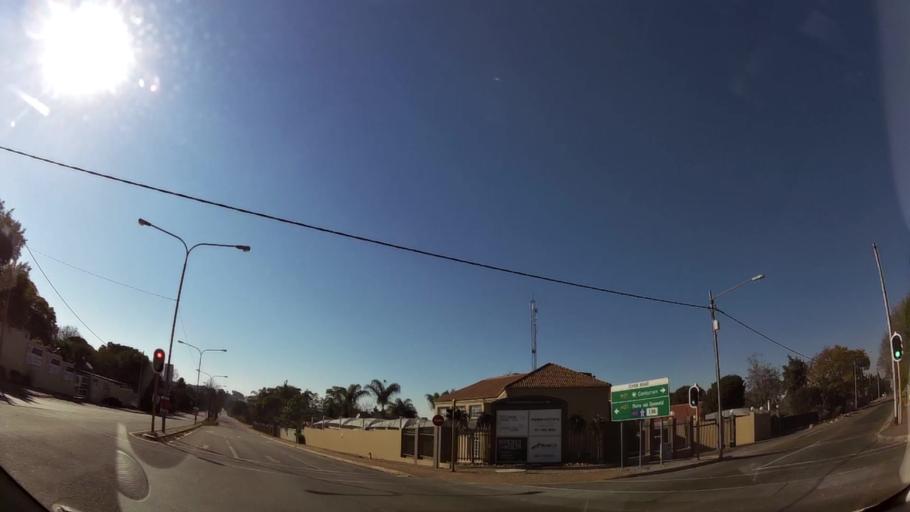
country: ZA
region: Gauteng
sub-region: City of Tshwane Metropolitan Municipality
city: Centurion
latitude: -25.8424
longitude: 28.2070
